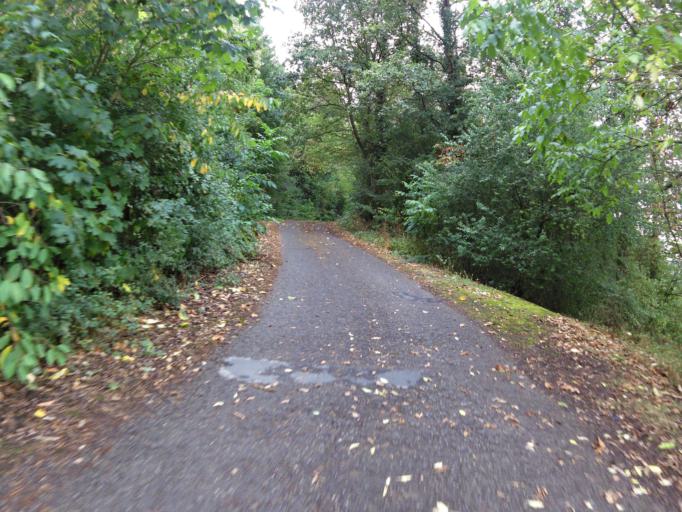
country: DE
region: Bavaria
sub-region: Regierungsbezirk Unterfranken
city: Guntersleben
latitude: 49.8692
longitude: 9.9106
